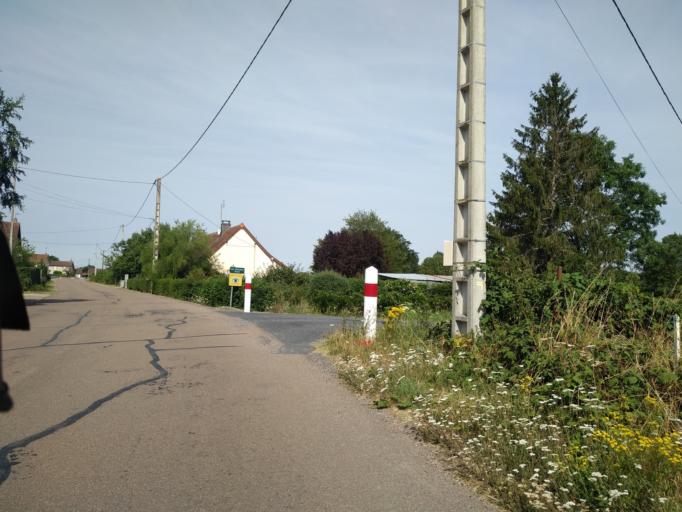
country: FR
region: Bourgogne
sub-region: Departement de Saone-et-Loire
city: Saint-Yan
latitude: 46.3488
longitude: 4.0273
